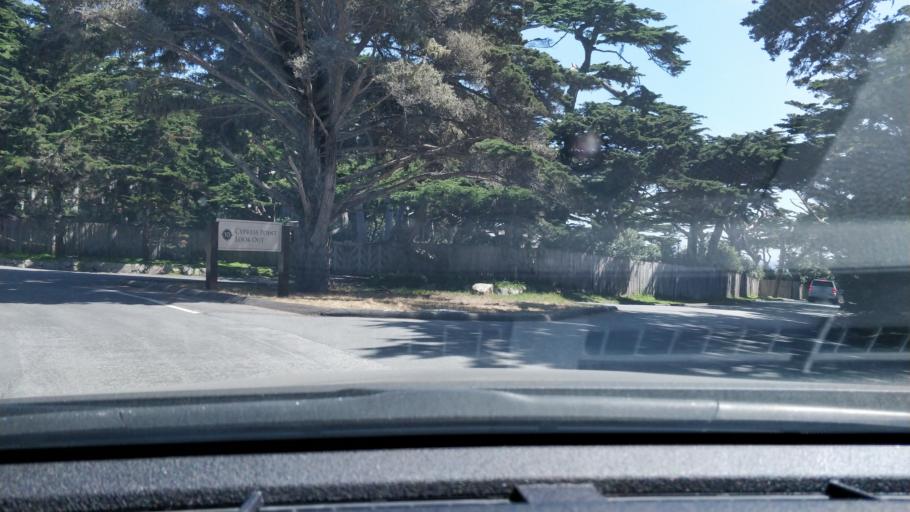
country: US
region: California
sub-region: Monterey County
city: Del Monte Forest
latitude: 36.5782
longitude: -121.9735
